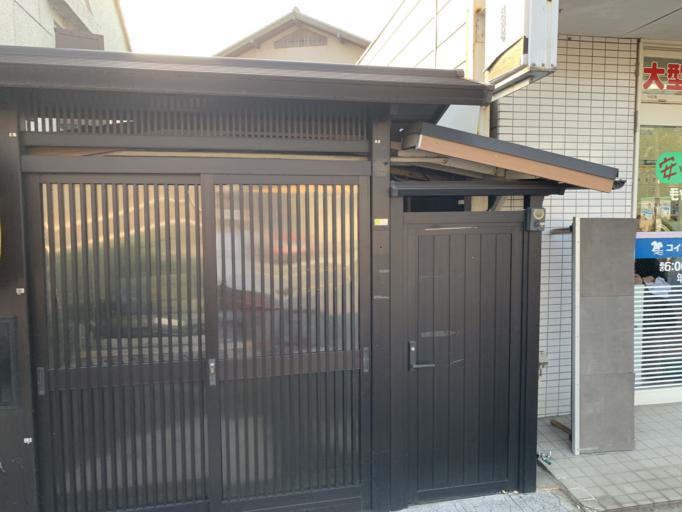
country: JP
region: Tokyo
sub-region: Machida-shi
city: Machida
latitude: 35.5720
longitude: 139.3840
